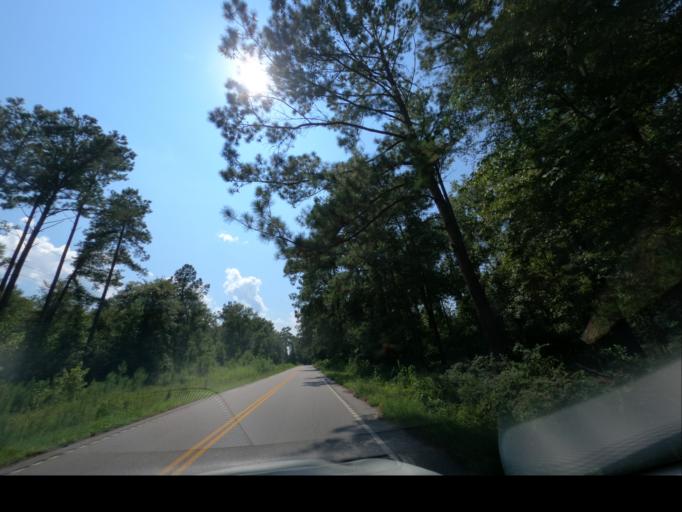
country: US
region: South Carolina
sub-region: Richland County
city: Hopkins
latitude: 33.8404
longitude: -80.8424
